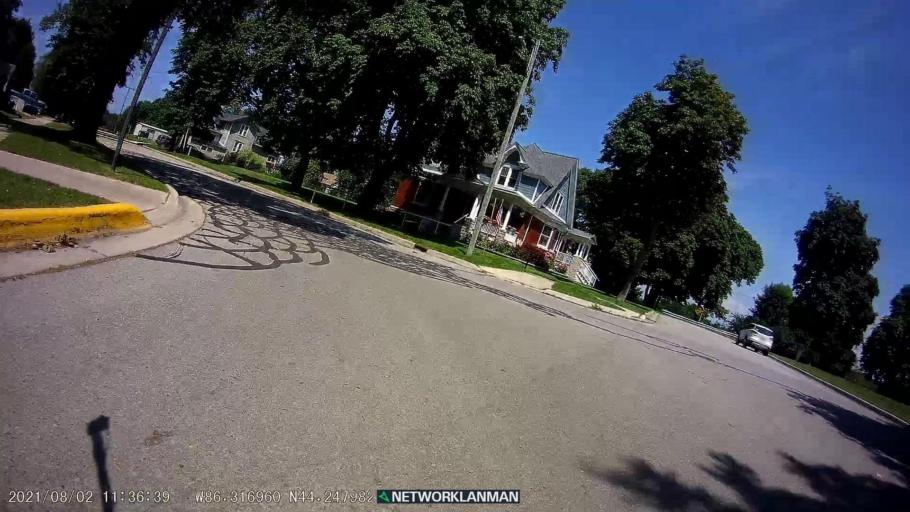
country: US
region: Michigan
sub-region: Manistee County
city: Manistee
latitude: 44.2479
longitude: -86.3170
